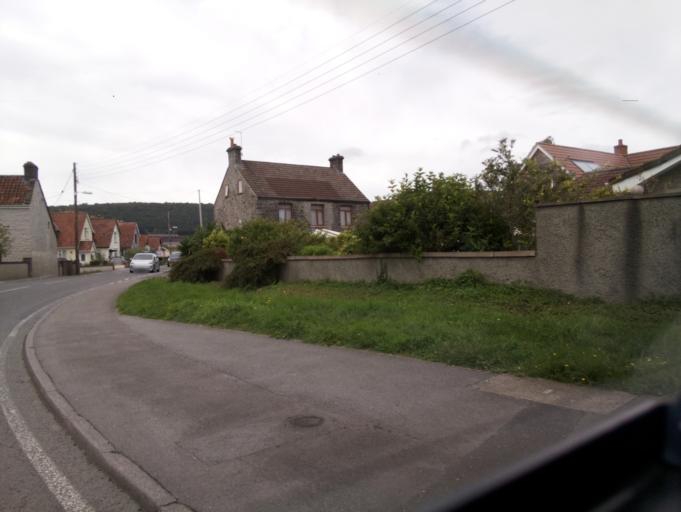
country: GB
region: England
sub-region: Somerset
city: Cheddar
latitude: 51.2783
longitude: -2.7885
